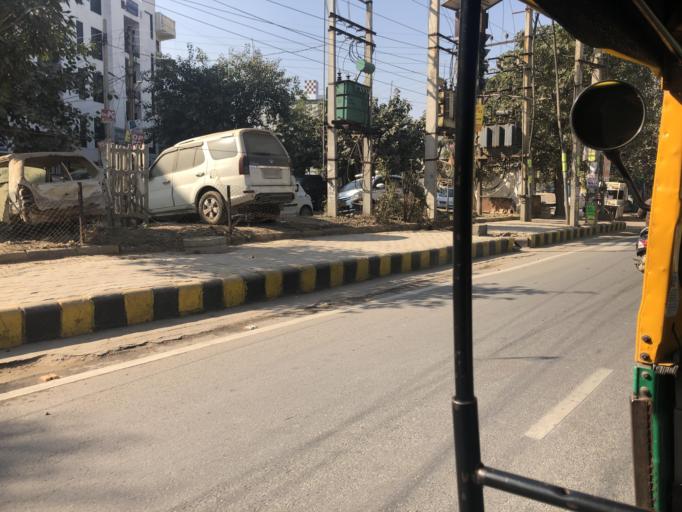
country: IN
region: Haryana
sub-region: Gurgaon
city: Gurgaon
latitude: 28.4490
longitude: 77.0722
